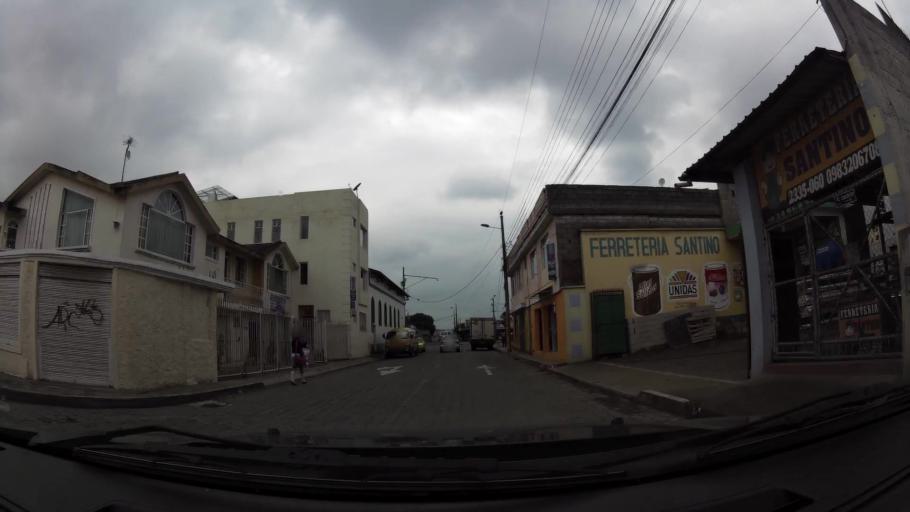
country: EC
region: Pichincha
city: Sangolqui
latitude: -0.3363
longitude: -78.4715
